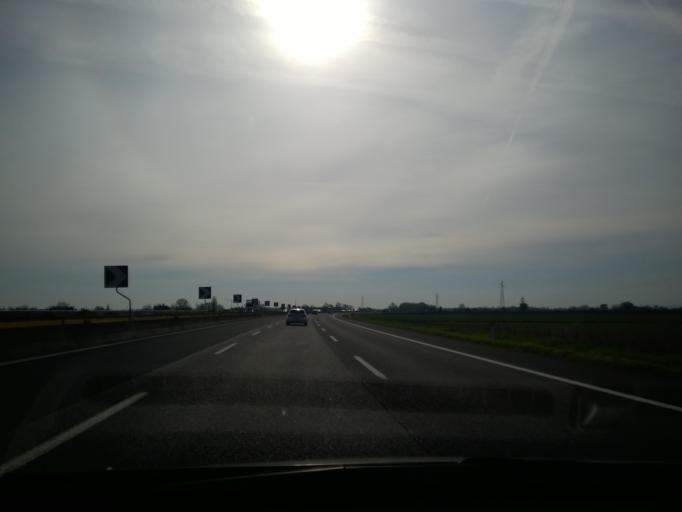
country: IT
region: Emilia-Romagna
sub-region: Forli-Cesena
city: Forli
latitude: 44.2811
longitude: 12.0174
